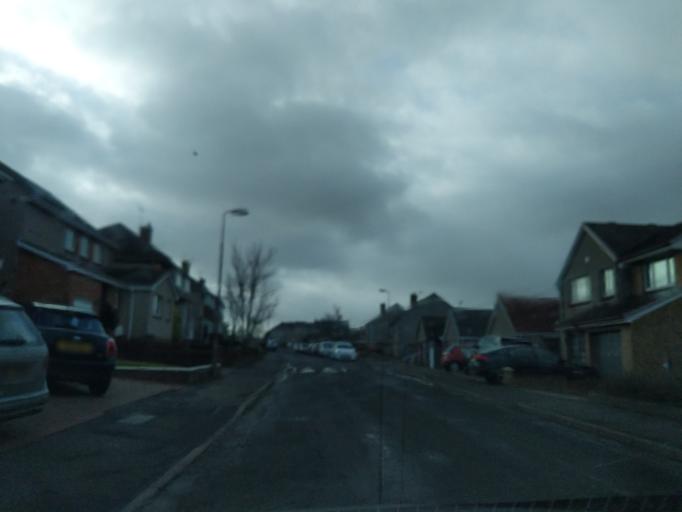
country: GB
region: Scotland
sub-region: Edinburgh
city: Currie
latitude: 55.8996
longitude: -3.3003
